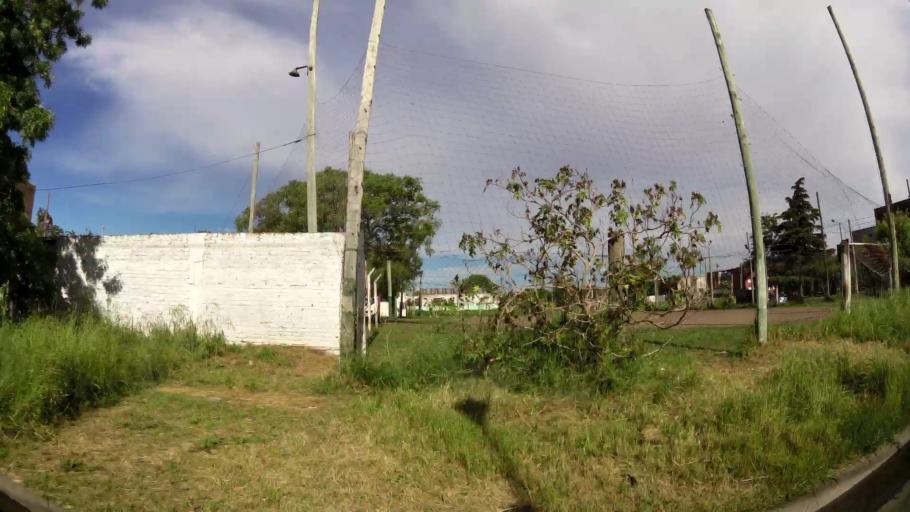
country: AR
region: Buenos Aires
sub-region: Partido de Almirante Brown
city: Adrogue
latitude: -34.8215
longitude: -58.3474
